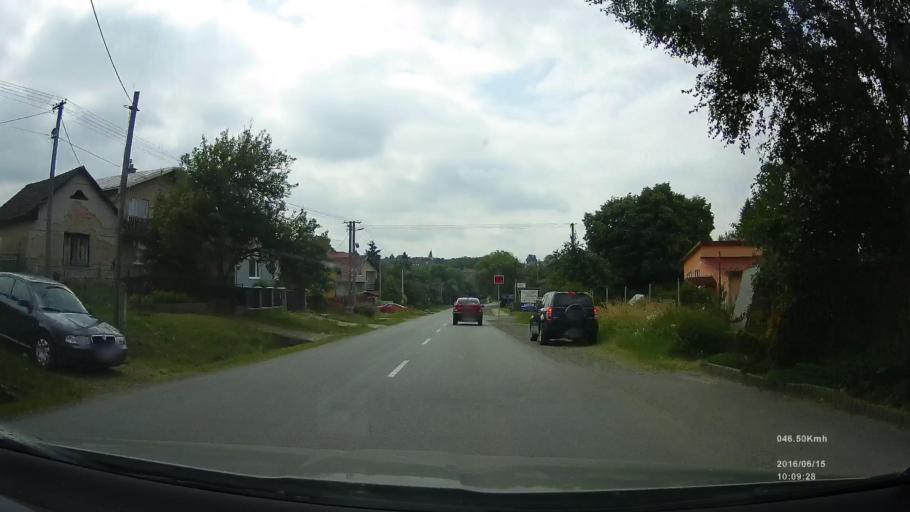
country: SK
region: Kosicky
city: Kosice
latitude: 48.7589
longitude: 21.3402
